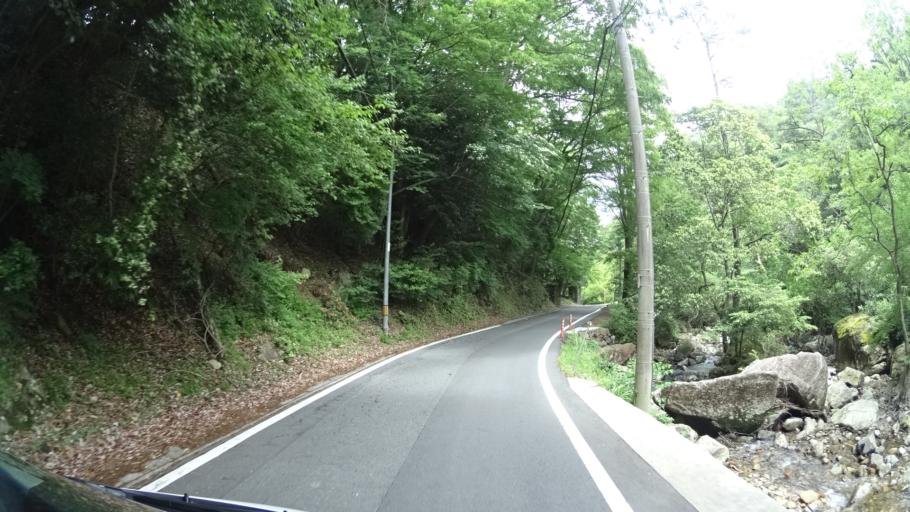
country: JP
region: Kyoto
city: Kameoka
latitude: 35.0438
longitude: 135.4112
